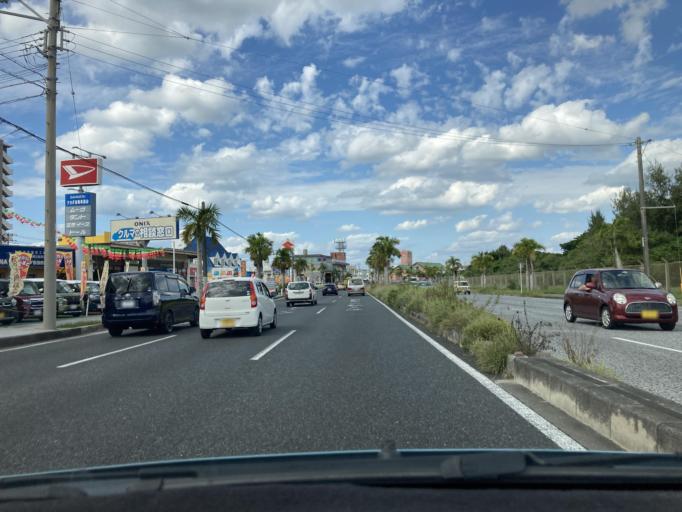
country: JP
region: Okinawa
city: Chatan
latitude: 26.3530
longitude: 127.7460
